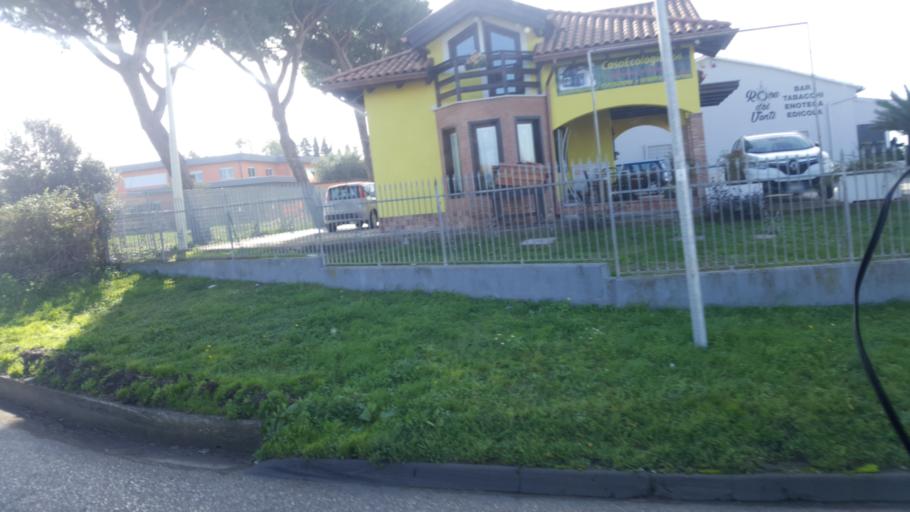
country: IT
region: Latium
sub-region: Provincia di Latina
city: Casalazzara
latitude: 41.6222
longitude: 12.5808
